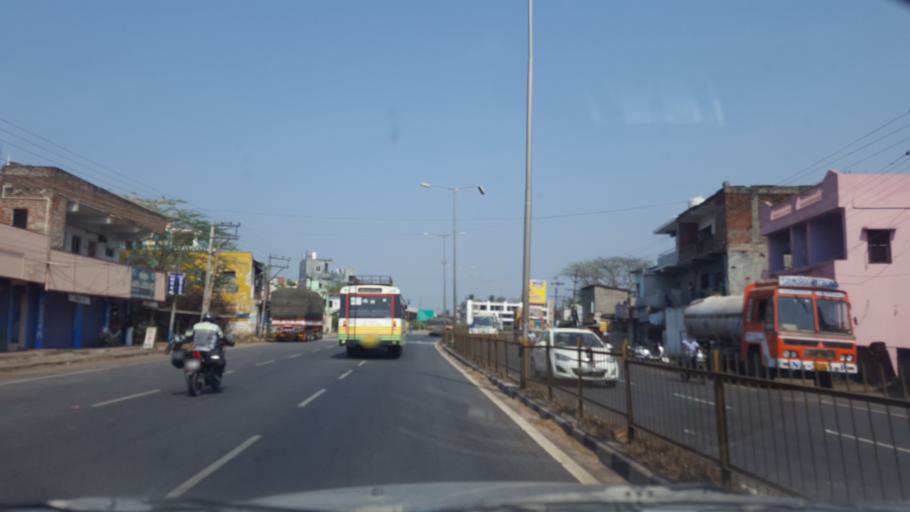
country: IN
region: Andhra Pradesh
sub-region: Vishakhapatnam
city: Anakapalle
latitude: 17.6830
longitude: 82.9841
